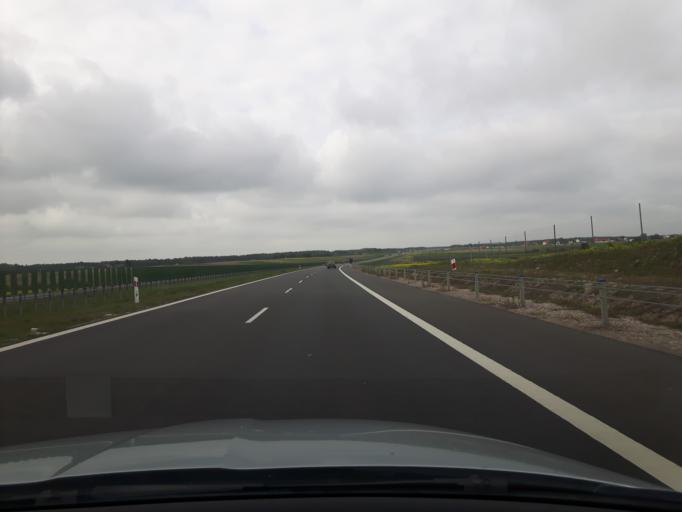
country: PL
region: Swietokrzyskie
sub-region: Powiat jedrzejowski
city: Sobkow
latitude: 50.6966
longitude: 20.3909
